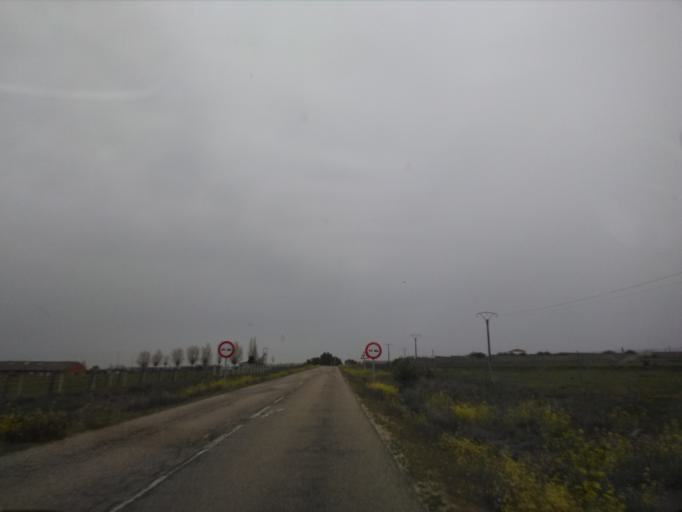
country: ES
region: Castille and Leon
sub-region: Provincia de Salamanca
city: Vitigudino
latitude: 40.9990
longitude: -6.4432
